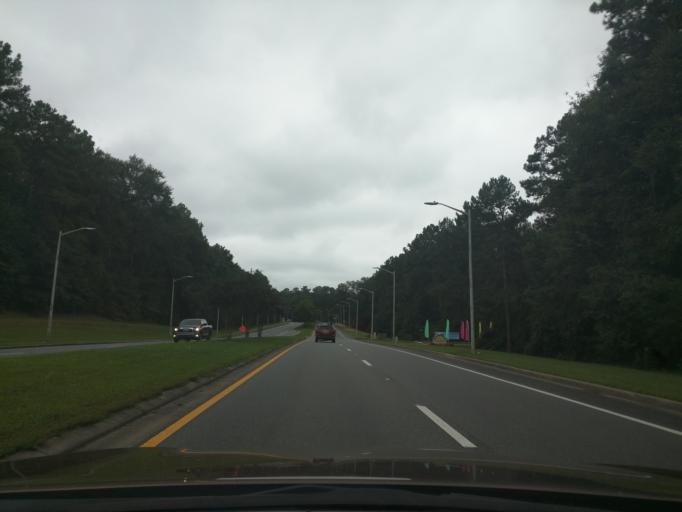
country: US
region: Florida
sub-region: Leon County
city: Tallahassee
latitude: 30.4329
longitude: -84.2016
